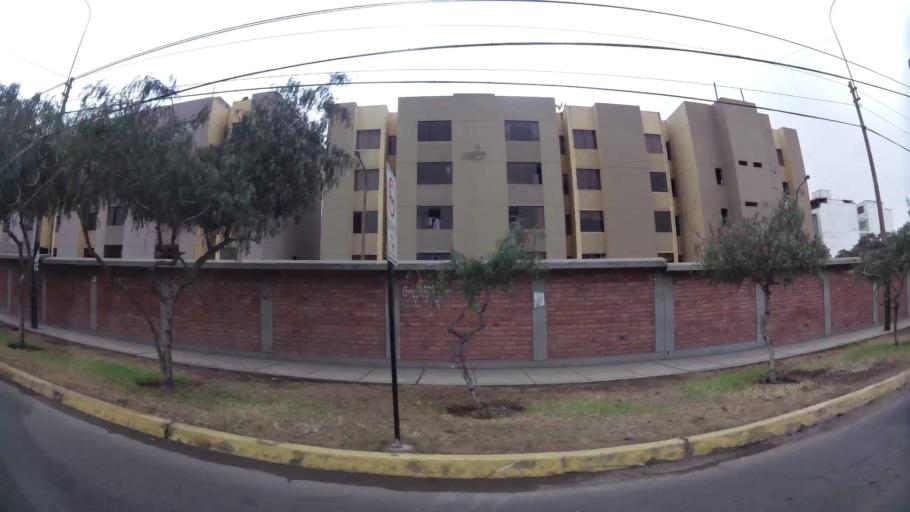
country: PE
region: Lima
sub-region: Lima
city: La Molina
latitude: -12.1043
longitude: -76.9643
